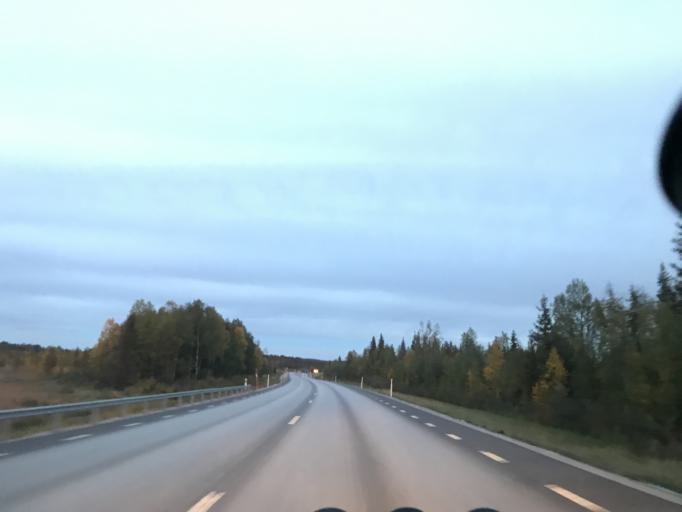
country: SE
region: Norrbotten
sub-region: Gallivare Kommun
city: Malmberget
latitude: 67.6466
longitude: 21.0308
